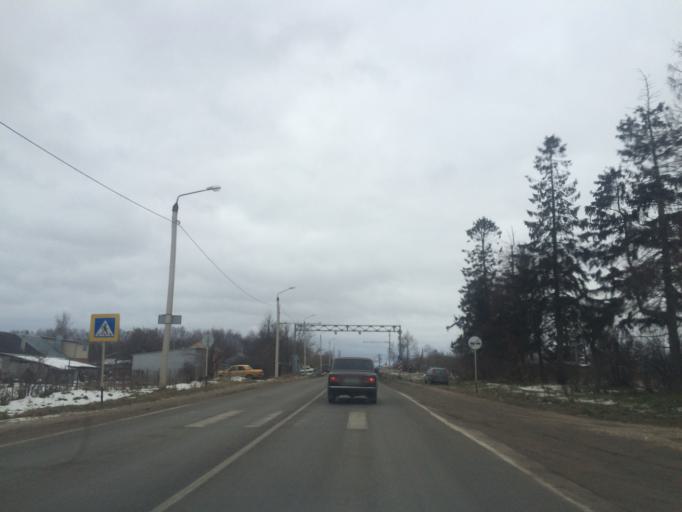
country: RU
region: Tula
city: Dubna
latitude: 54.1069
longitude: 37.1135
